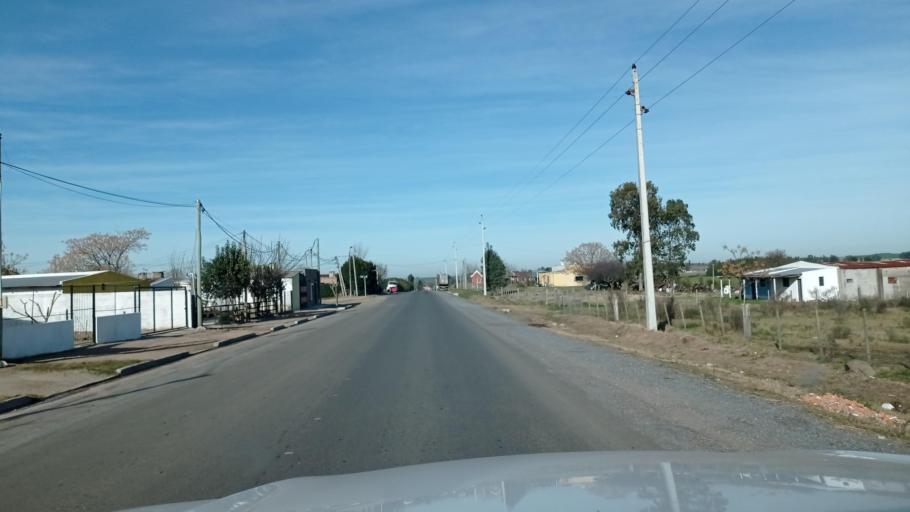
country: UY
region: Florida
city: Florida
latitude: -34.0979
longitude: -56.2409
